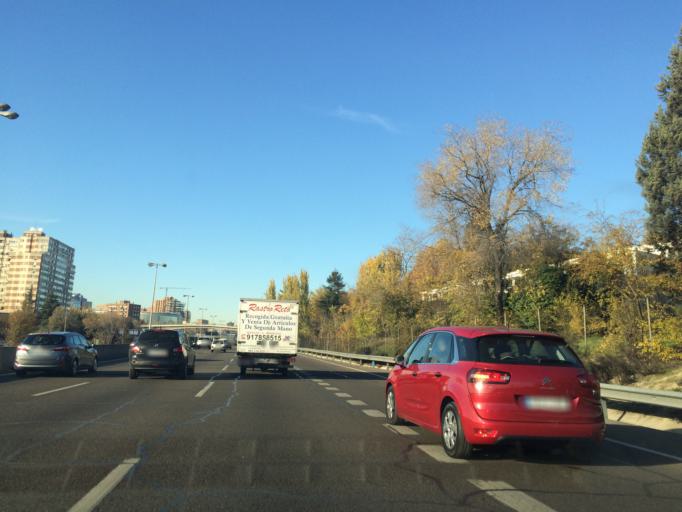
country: ES
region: Madrid
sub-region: Provincia de Madrid
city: Chamartin
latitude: 40.4607
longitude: -3.6647
